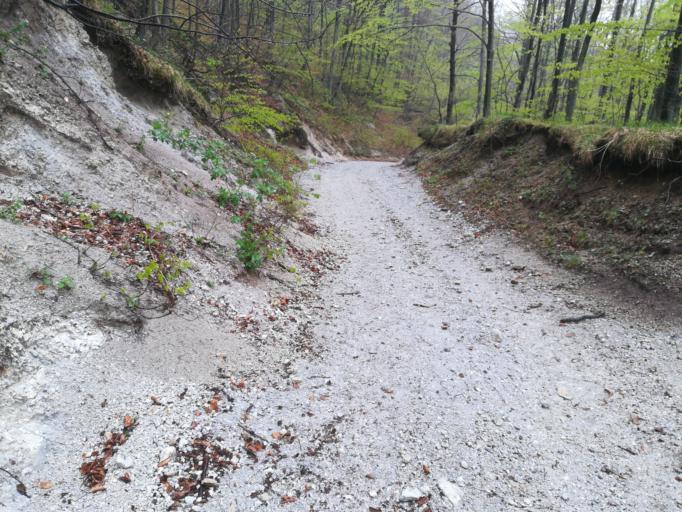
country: HR
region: Varazdinska
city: Ivanec
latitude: 46.1900
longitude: 16.1470
